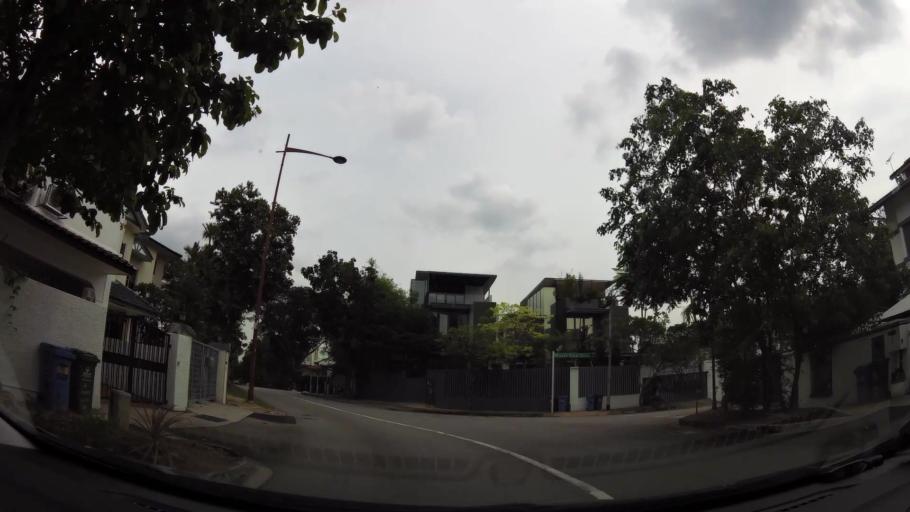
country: SG
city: Singapore
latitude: 1.3159
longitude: 103.7821
